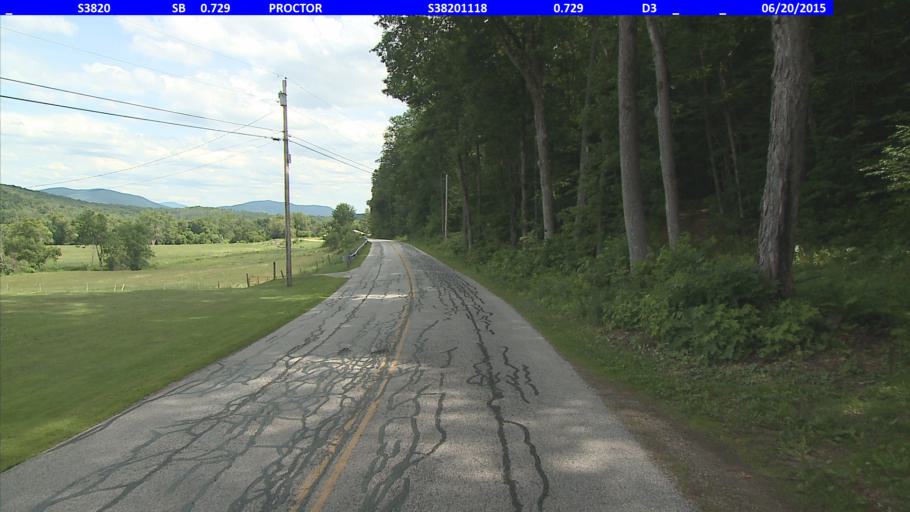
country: US
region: Vermont
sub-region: Rutland County
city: West Rutland
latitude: 43.6203
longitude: -73.0329
